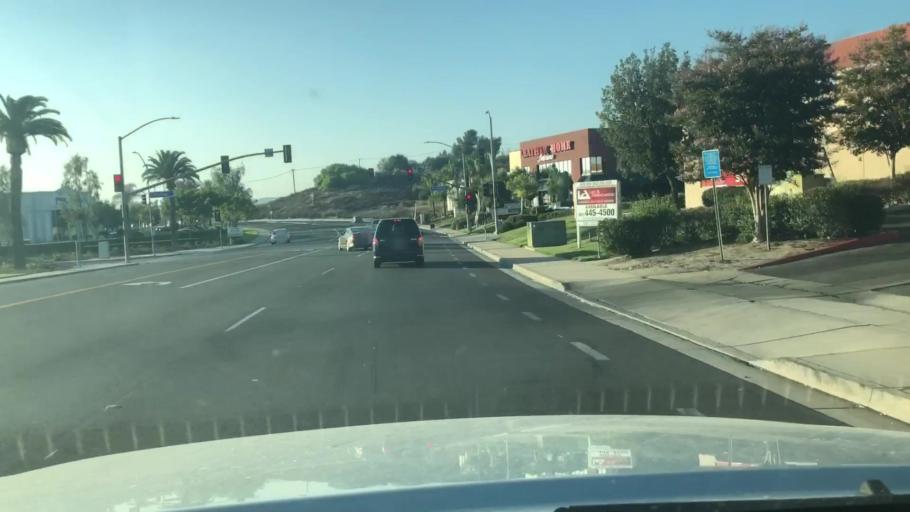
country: US
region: California
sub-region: Riverside County
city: Murrieta Hot Springs
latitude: 33.5330
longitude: -117.1780
